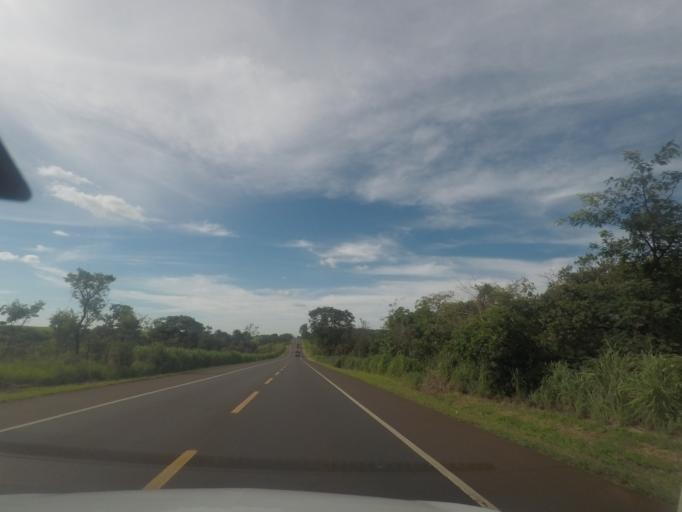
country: BR
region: Minas Gerais
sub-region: Monte Alegre De Minas
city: Monte Alegre de Minas
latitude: -19.0072
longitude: -49.0184
